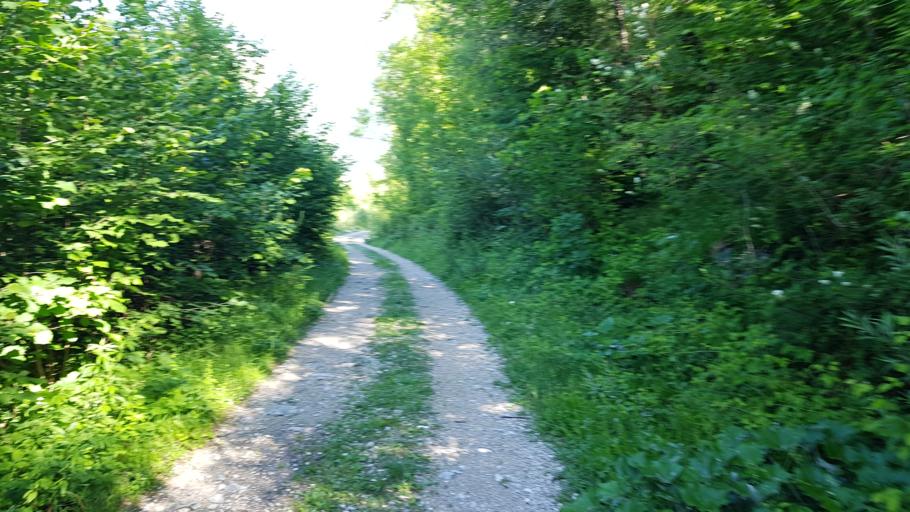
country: SI
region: Bovec
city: Bovec
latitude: 46.2990
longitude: 13.4969
